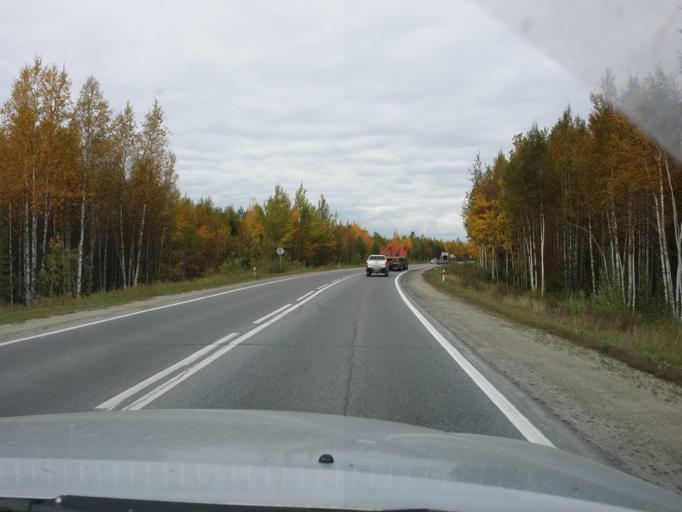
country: RU
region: Khanty-Mansiyskiy Avtonomnyy Okrug
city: Langepas
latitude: 61.1584
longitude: 75.6069
